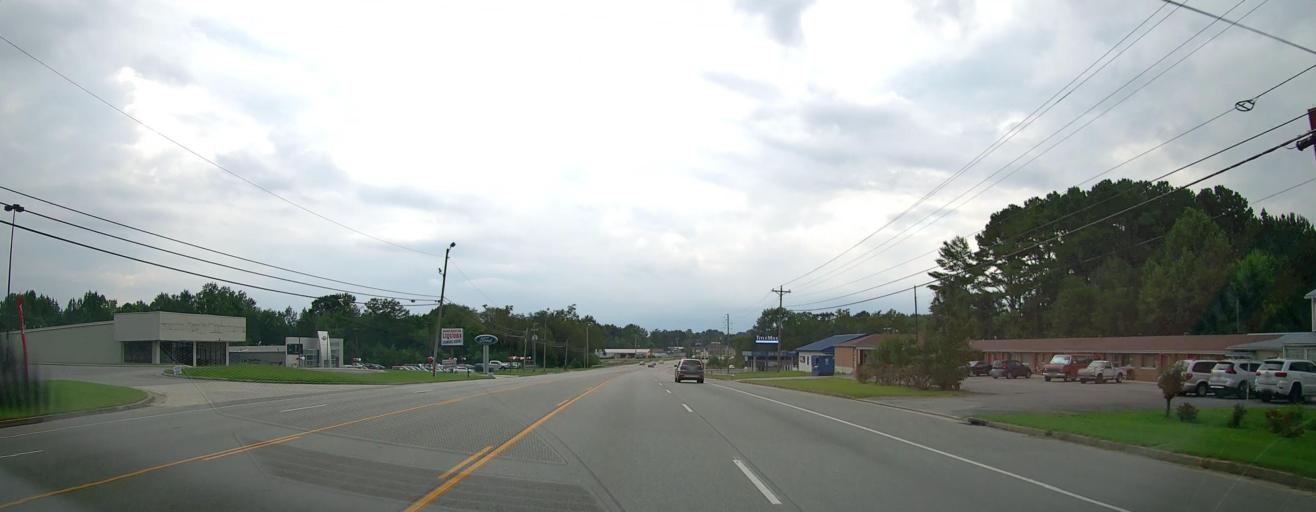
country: US
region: Tennessee
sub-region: Coffee County
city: Manchester
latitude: 35.4612
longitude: -86.0619
